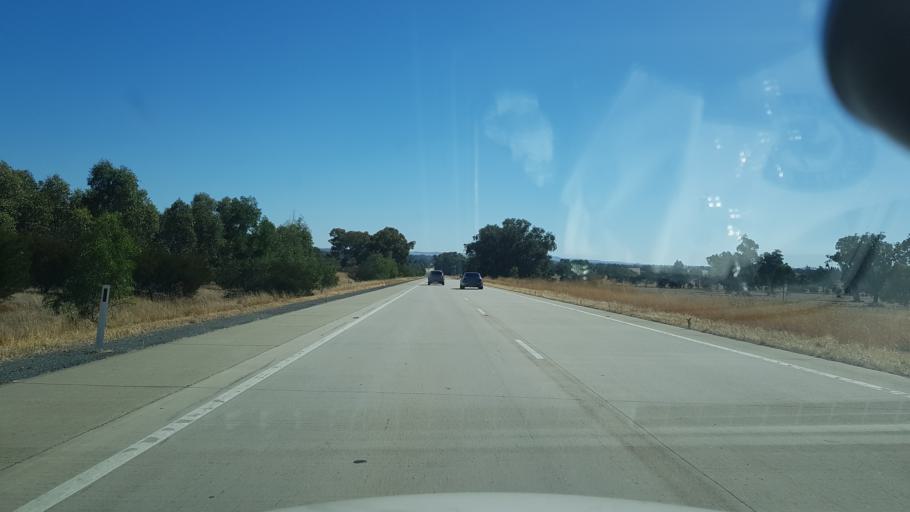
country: AU
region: New South Wales
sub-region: Greater Hume Shire
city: Jindera
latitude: -35.9246
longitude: 147.0484
